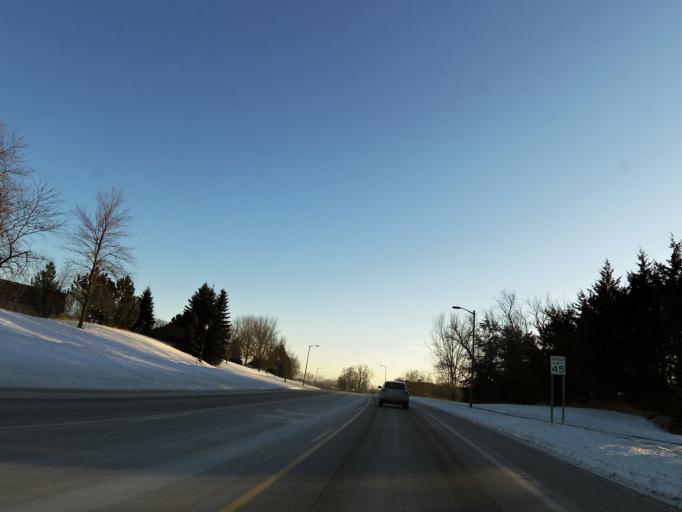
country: US
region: Minnesota
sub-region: Hennepin County
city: Shorewood
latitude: 44.8530
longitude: -93.5822
